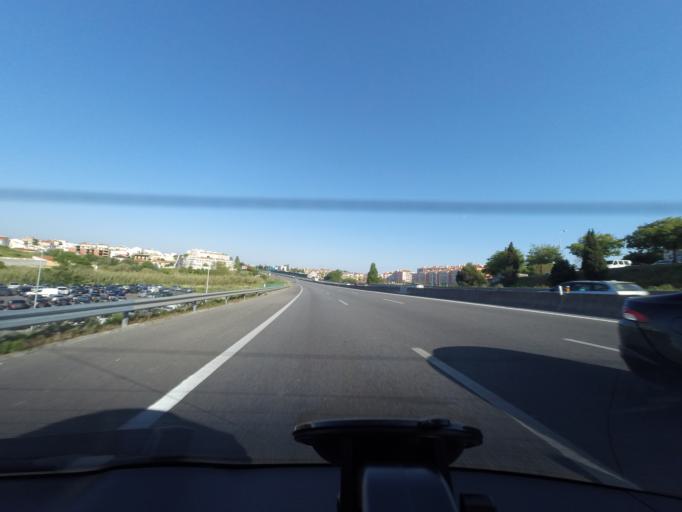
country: PT
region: Lisbon
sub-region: Cascais
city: Parede
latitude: 38.7090
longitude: -9.3484
